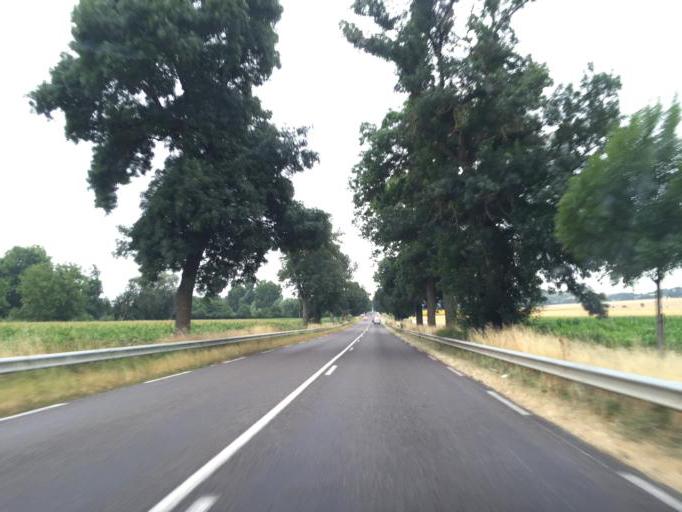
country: FR
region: Auvergne
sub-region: Departement de l'Allier
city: Gannat
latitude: 46.1332
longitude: 3.2101
